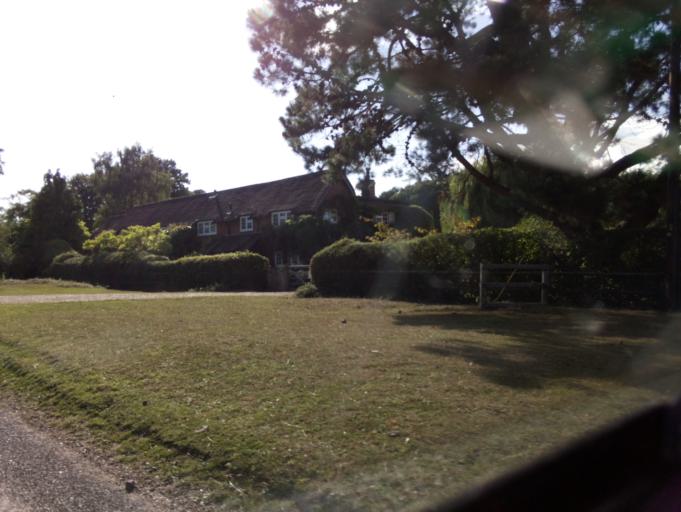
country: GB
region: England
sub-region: Hampshire
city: Cadnam
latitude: 50.9420
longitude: -1.6005
